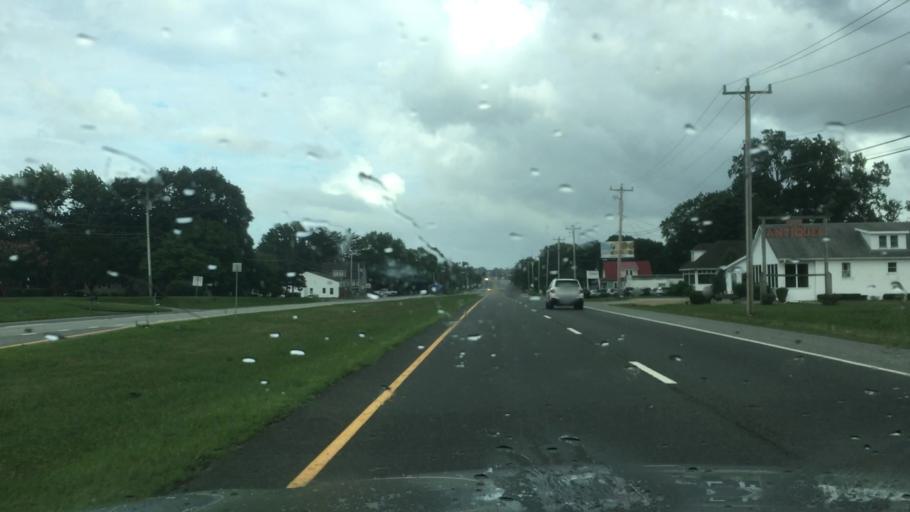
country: US
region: Delaware
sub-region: Kent County
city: Smyrna
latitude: 39.3129
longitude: -75.6129
